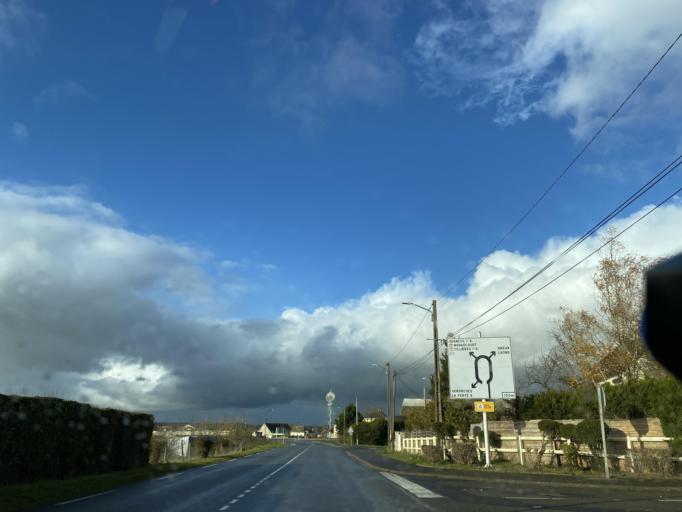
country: FR
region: Centre
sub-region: Departement d'Eure-et-Loir
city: Brezolles
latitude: 48.6879
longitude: 1.0816
